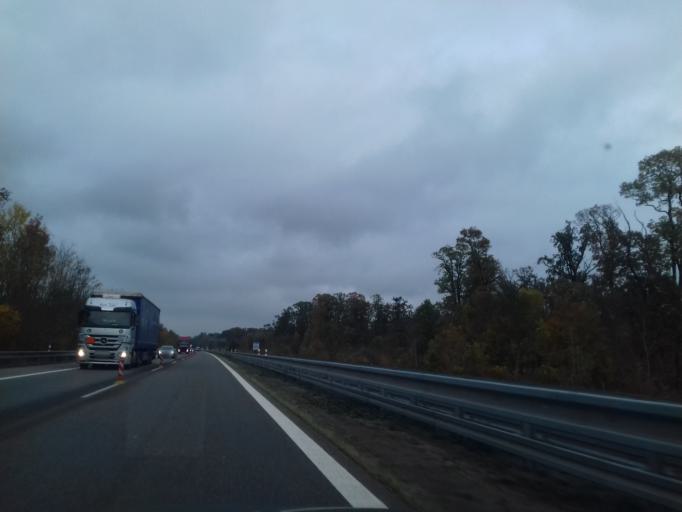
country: CZ
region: South Moravian
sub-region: Okres Breclav
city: Lanzhot
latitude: 48.7053
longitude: 16.9873
